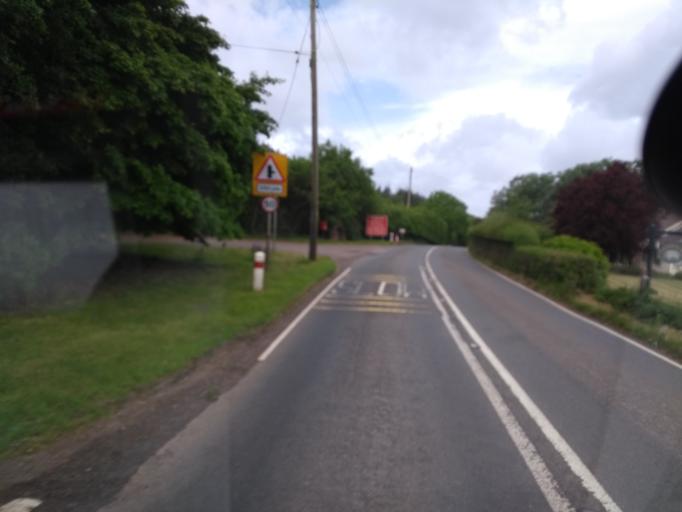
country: GB
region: England
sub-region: Somerset
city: Bishops Lydeard
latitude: 51.1525
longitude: -3.1820
